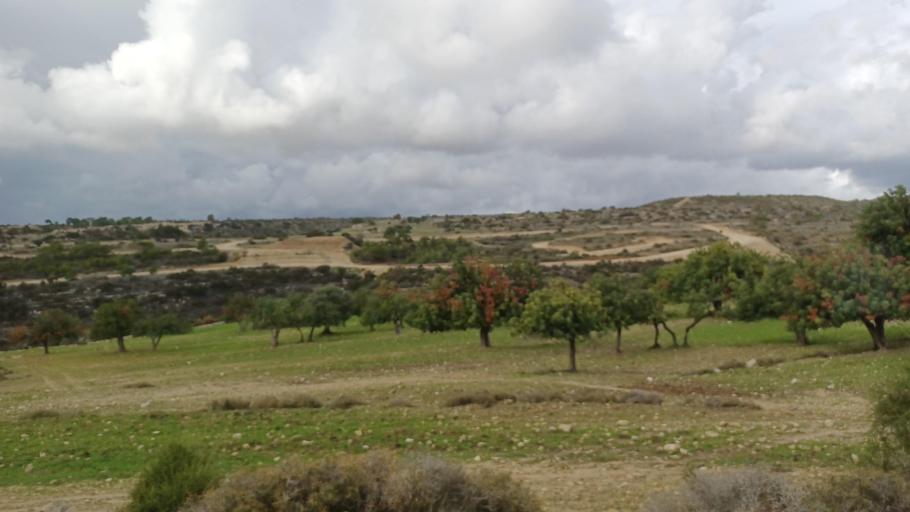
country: CY
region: Limassol
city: Sotira
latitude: 34.7267
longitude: 32.8196
